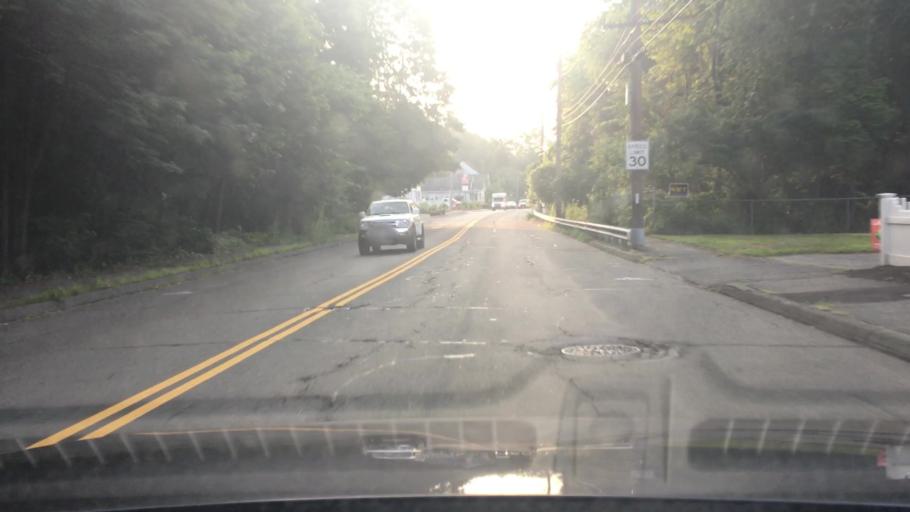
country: US
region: Massachusetts
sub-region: Essex County
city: Saugus
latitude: 42.4741
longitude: -70.9917
